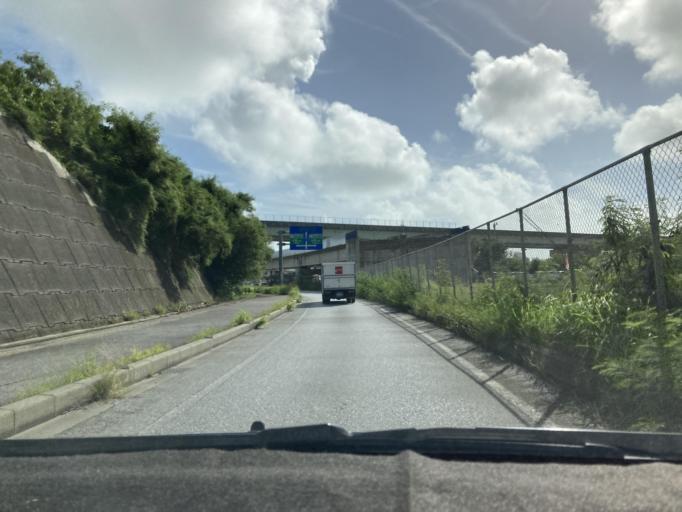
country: JP
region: Okinawa
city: Naha-shi
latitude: 26.2024
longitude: 127.7375
